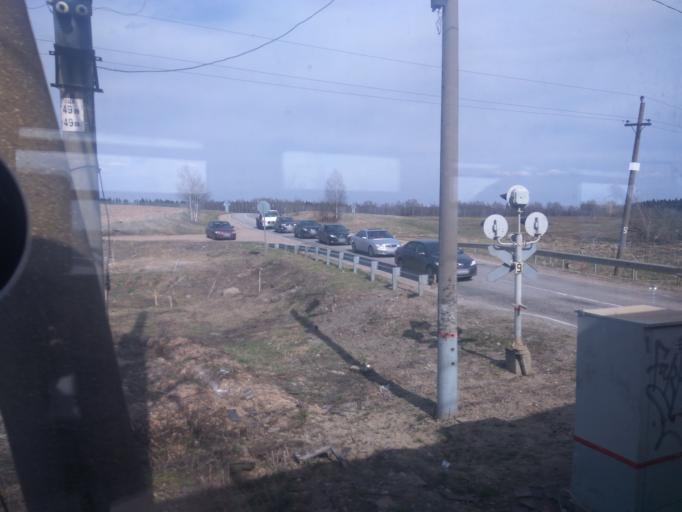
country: RU
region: Moskovskaya
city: Budenovetc
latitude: 56.3134
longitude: 37.7316
